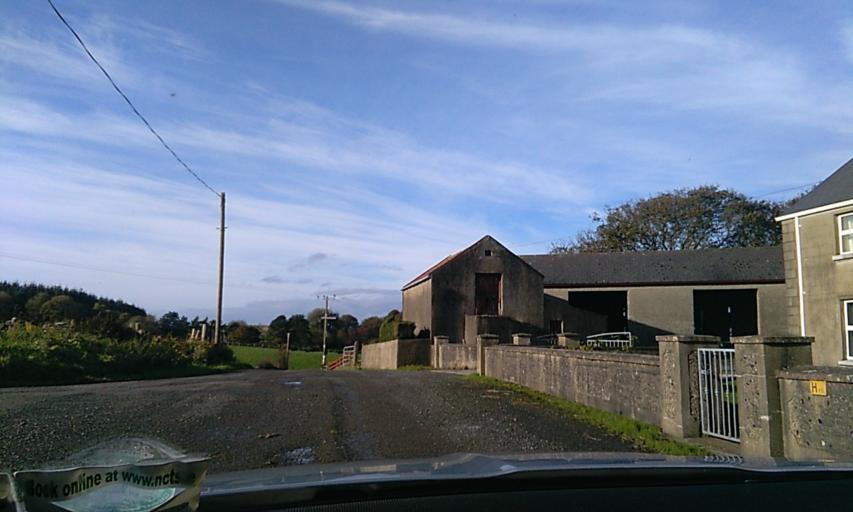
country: IE
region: Ulster
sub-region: County Donegal
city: Carndonagh
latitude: 55.2800
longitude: -7.1466
